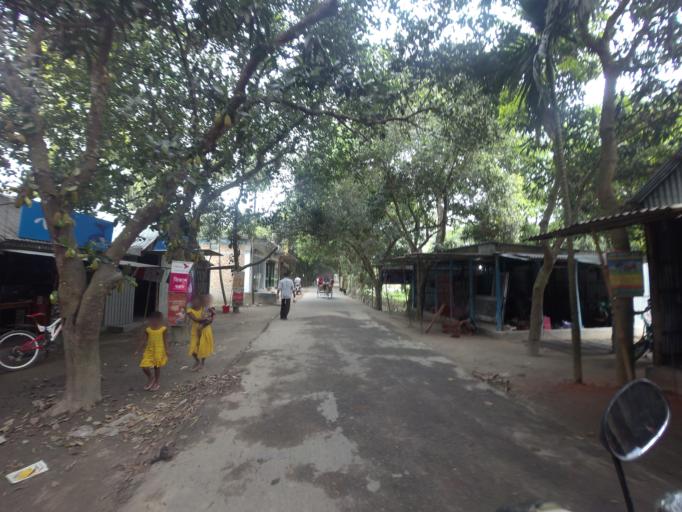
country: BD
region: Rajshahi
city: Sirajganj
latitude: 24.3374
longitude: 89.6847
